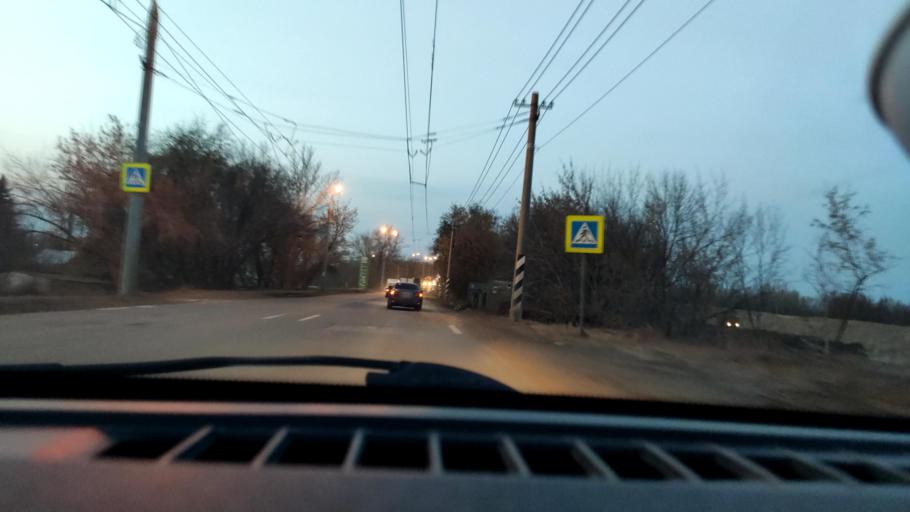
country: RU
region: Samara
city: Samara
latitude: 53.1474
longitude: 50.0954
